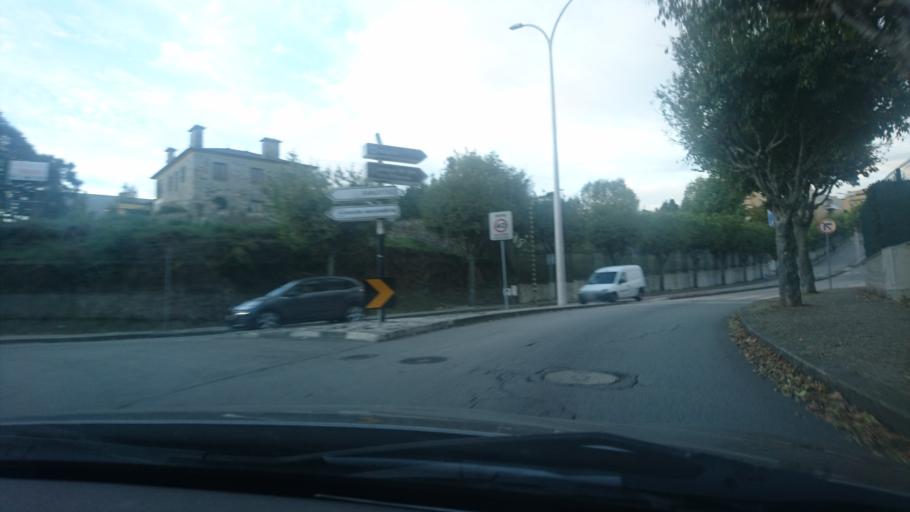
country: PT
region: Aveiro
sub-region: Sao Joao da Madeira
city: Sao Joao da Madeira
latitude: 40.8942
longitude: -8.4854
